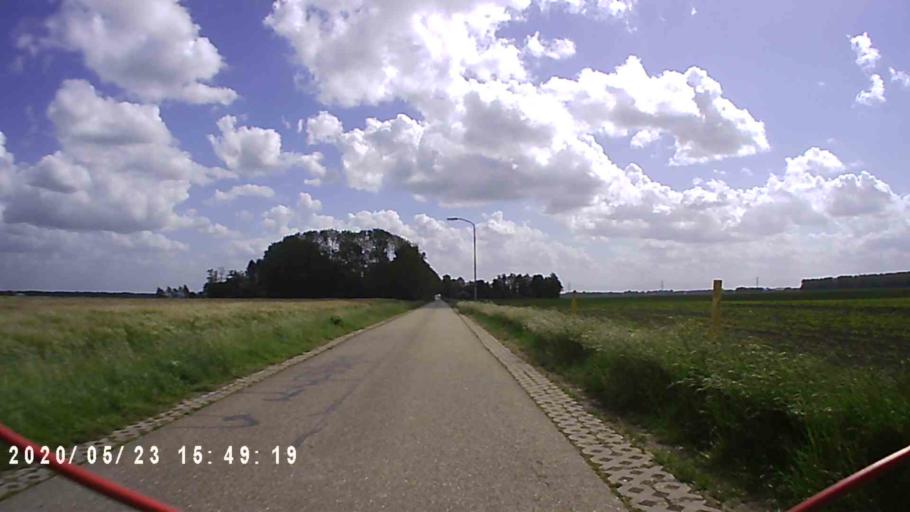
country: NL
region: Groningen
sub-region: Gemeente Delfzijl
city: Delfzijl
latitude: 53.2780
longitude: 6.9055
